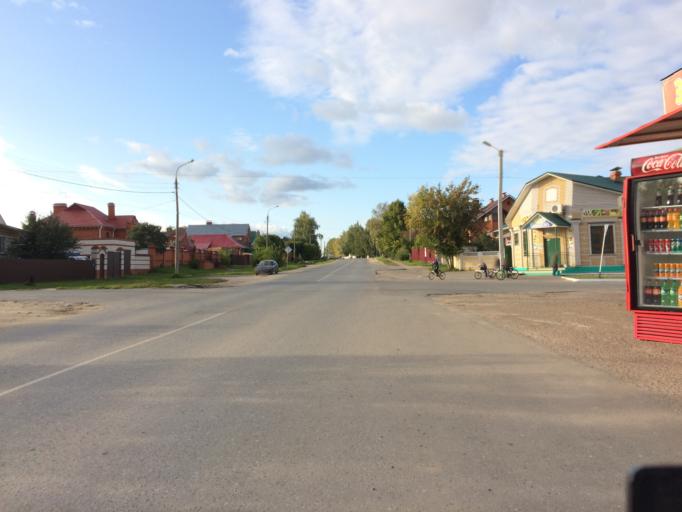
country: RU
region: Mariy-El
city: Yoshkar-Ola
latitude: 56.6505
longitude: 47.9801
